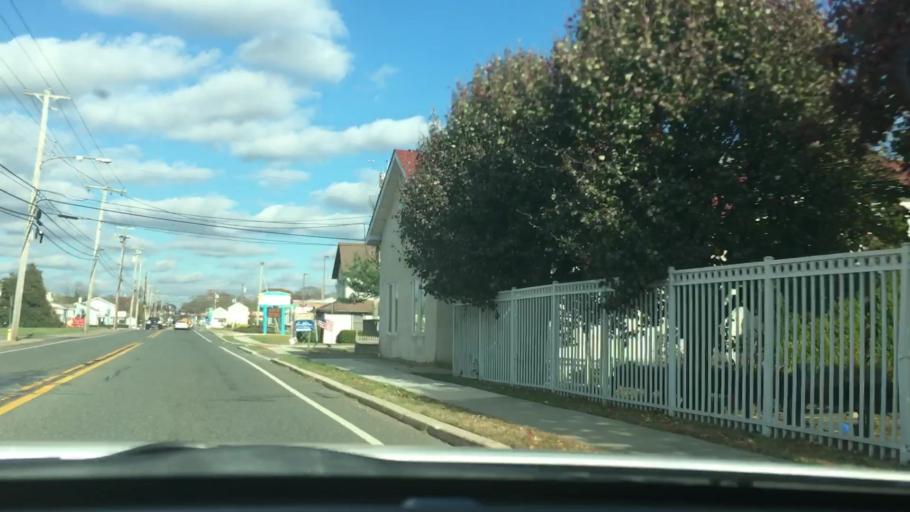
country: US
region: New Jersey
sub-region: Atlantic County
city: Northfield
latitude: 39.3724
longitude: -74.5563
